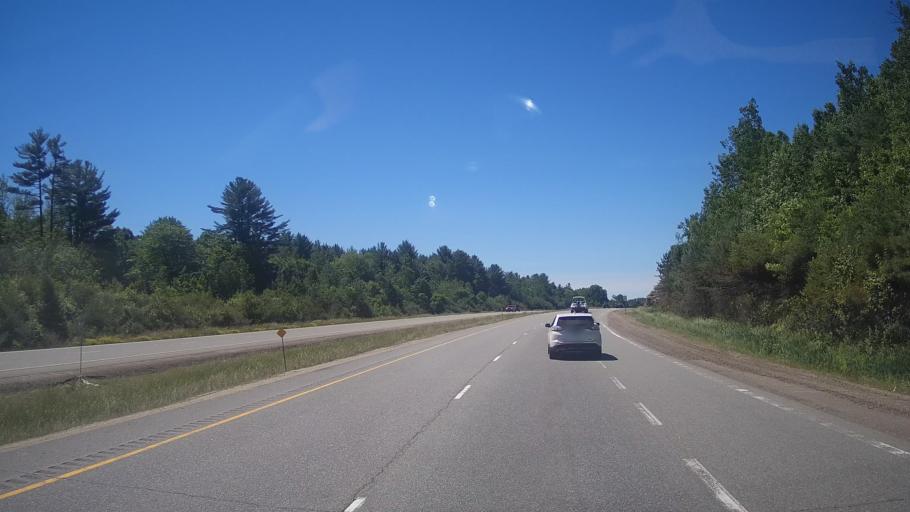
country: CA
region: Ontario
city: Bracebridge
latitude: 45.0459
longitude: -79.2870
